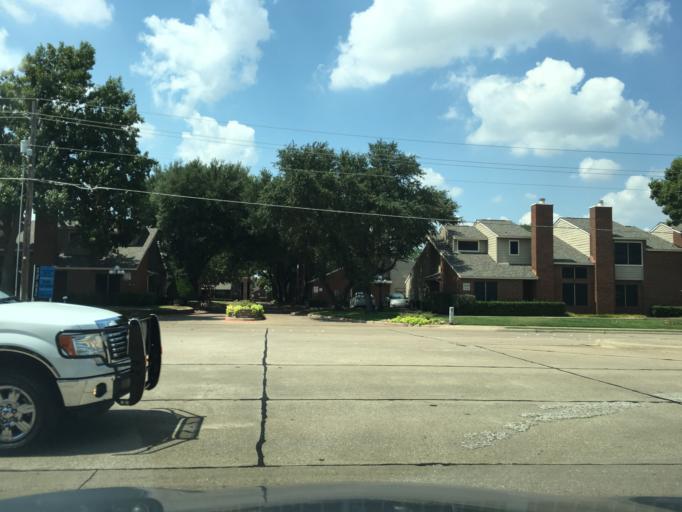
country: US
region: Texas
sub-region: Dallas County
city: Garland
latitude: 32.9417
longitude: -96.6479
